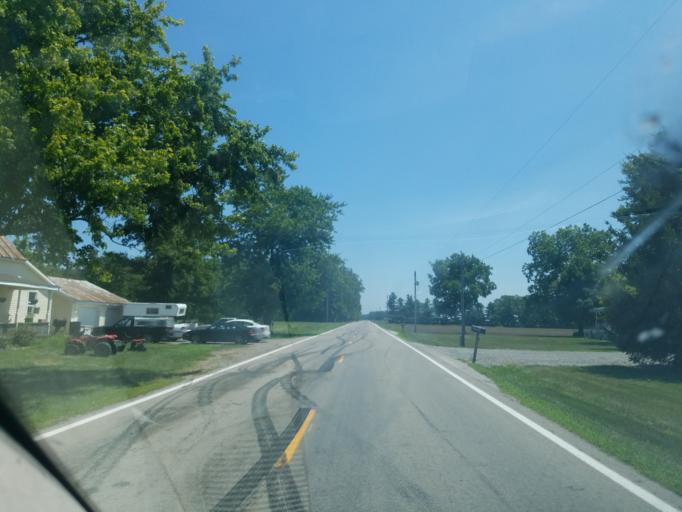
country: US
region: Ohio
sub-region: Allen County
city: Spencerville
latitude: 40.7430
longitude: -84.4124
